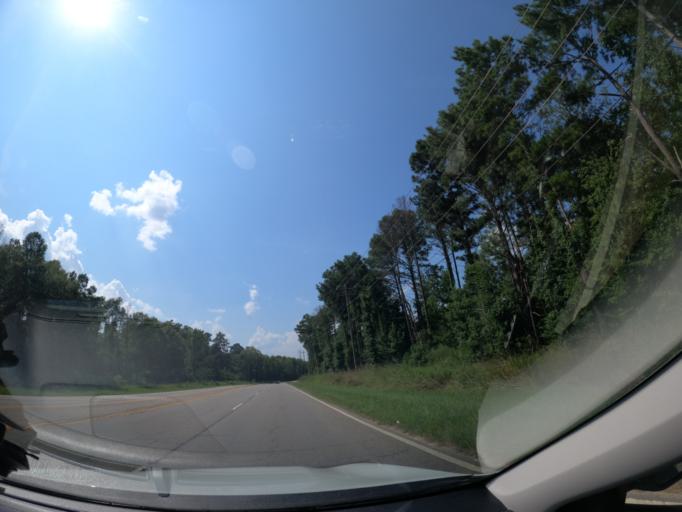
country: US
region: South Carolina
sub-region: Richland County
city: Forest Acres
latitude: 33.9398
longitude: -80.9823
